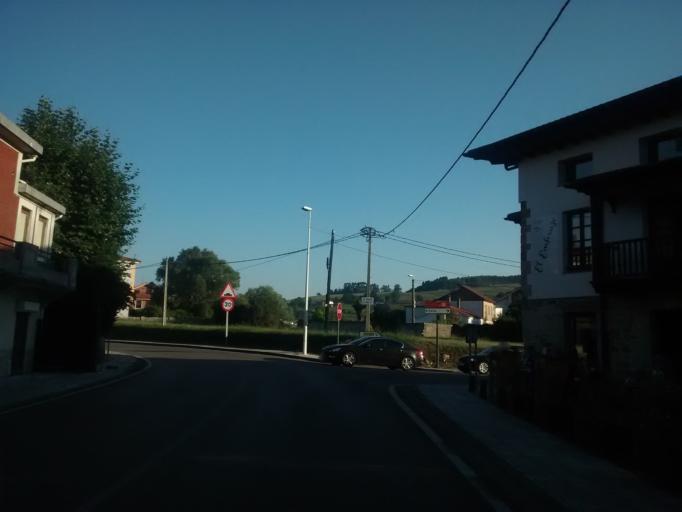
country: ES
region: Cantabria
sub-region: Provincia de Cantabria
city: San Miguel de Meruelo
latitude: 43.4555
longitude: -3.5754
